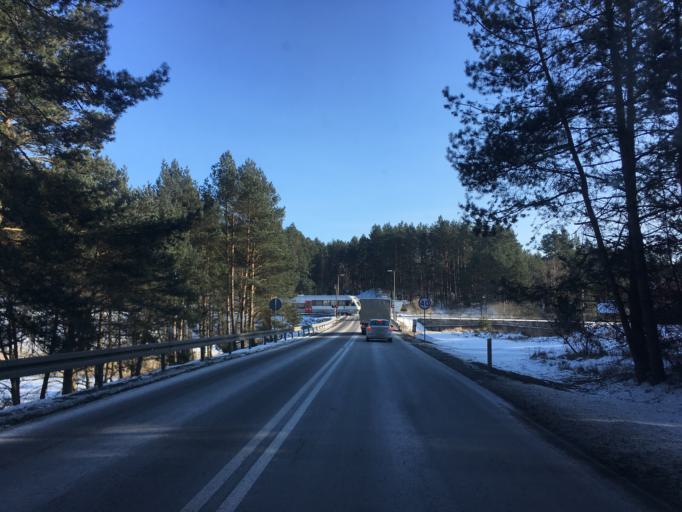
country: PL
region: Pomeranian Voivodeship
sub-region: Powiat koscierski
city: Koscierzyna
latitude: 54.1188
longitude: 17.8883
